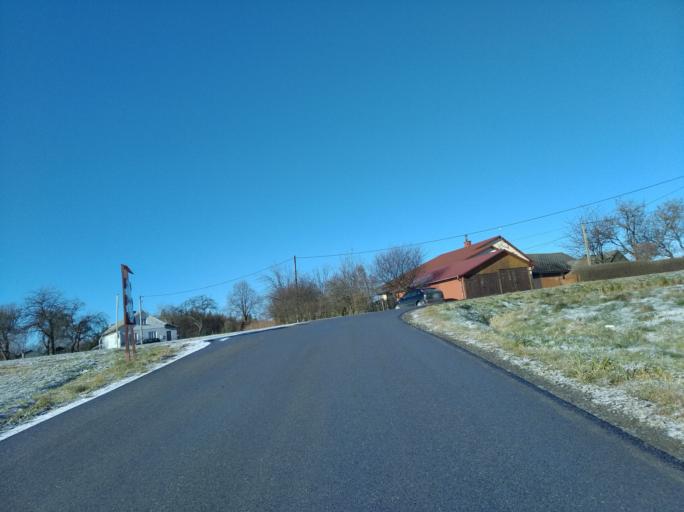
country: PL
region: Subcarpathian Voivodeship
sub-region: Powiat ropczycko-sedziszowski
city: Iwierzyce
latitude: 49.9678
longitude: 21.7501
